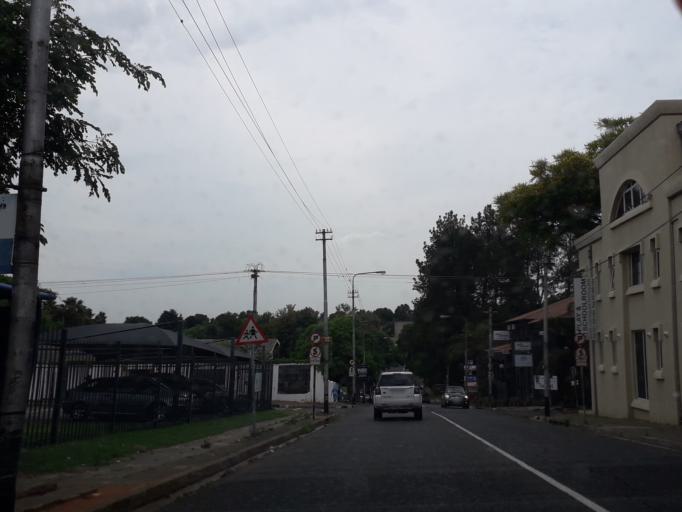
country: ZA
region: Gauteng
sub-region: City of Johannesburg Metropolitan Municipality
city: Johannesburg
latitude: -26.1494
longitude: 28.0774
